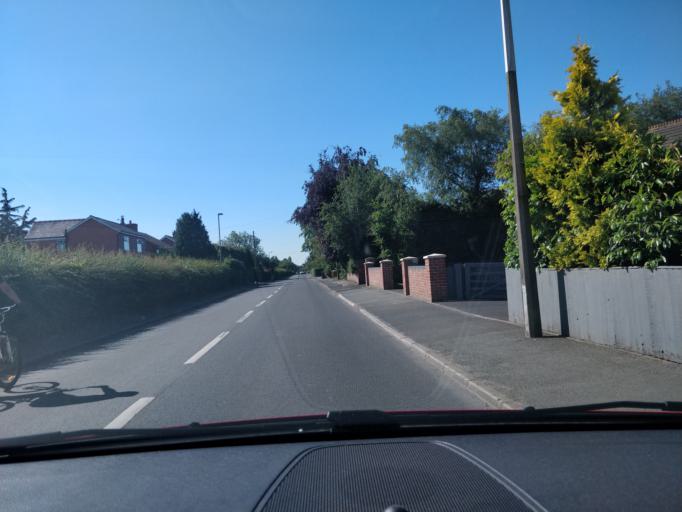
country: GB
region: England
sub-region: Lancashire
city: Tarleton
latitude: 53.7073
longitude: -2.8430
